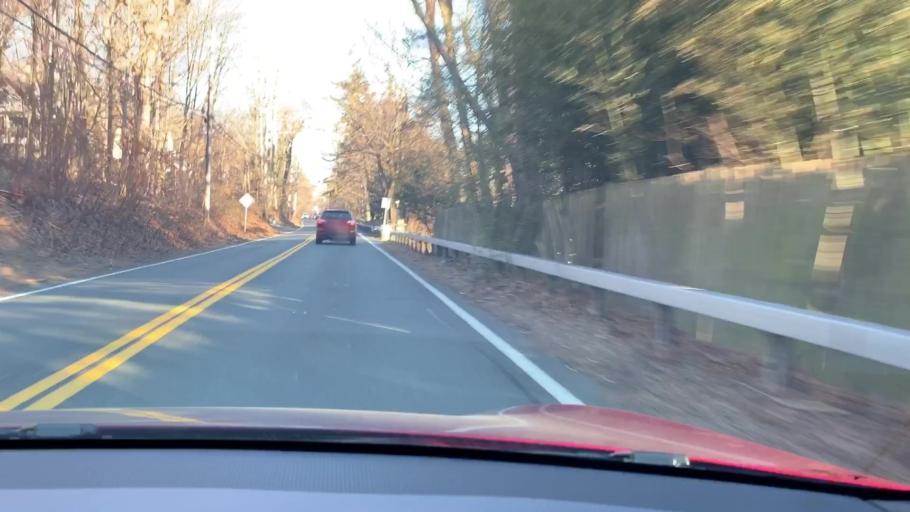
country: US
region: New York
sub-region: Rockland County
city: Piermont
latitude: 41.0432
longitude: -73.9209
